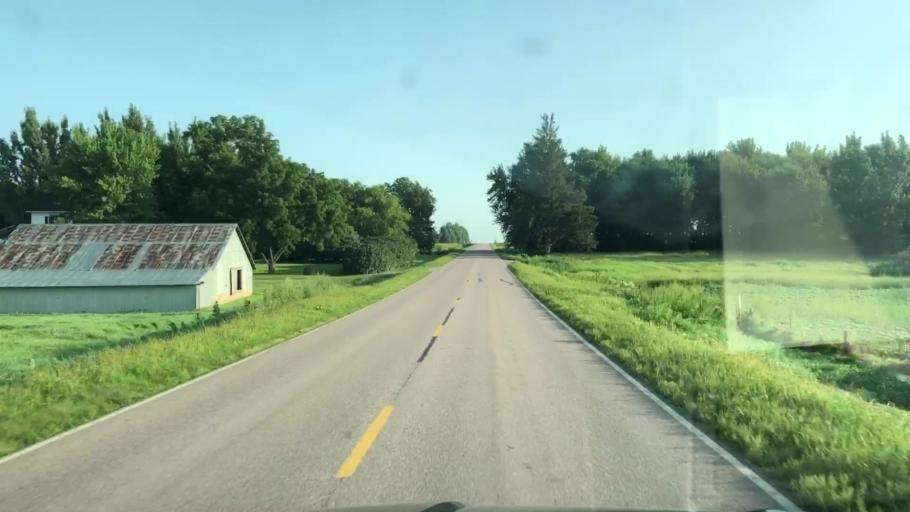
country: US
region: Iowa
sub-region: Lyon County
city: George
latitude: 43.2539
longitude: -96.0002
